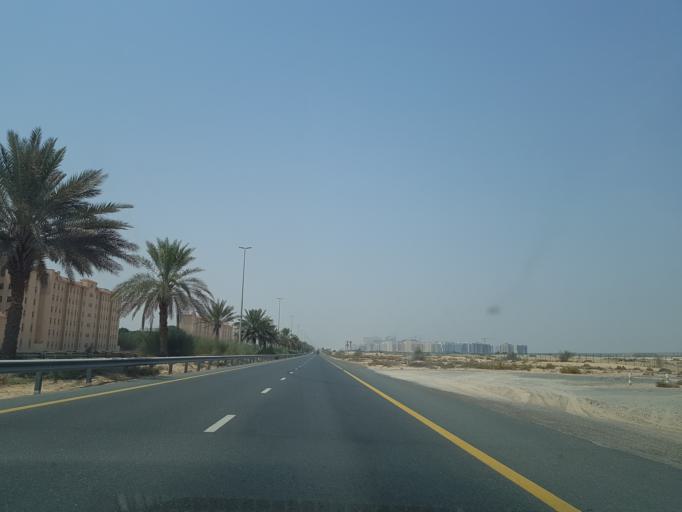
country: AE
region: Ash Shariqah
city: Sharjah
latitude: 25.1343
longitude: 55.4205
